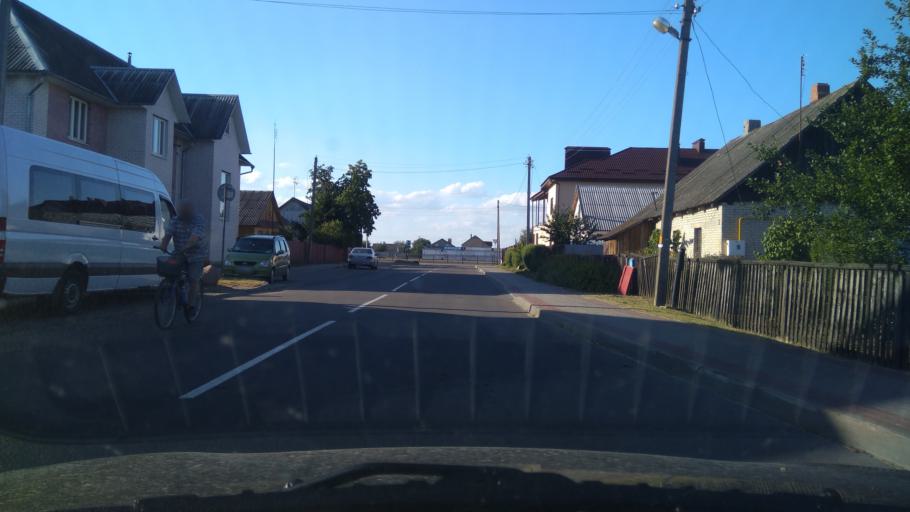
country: BY
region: Brest
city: Byaroza
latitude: 52.5396
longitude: 24.9781
